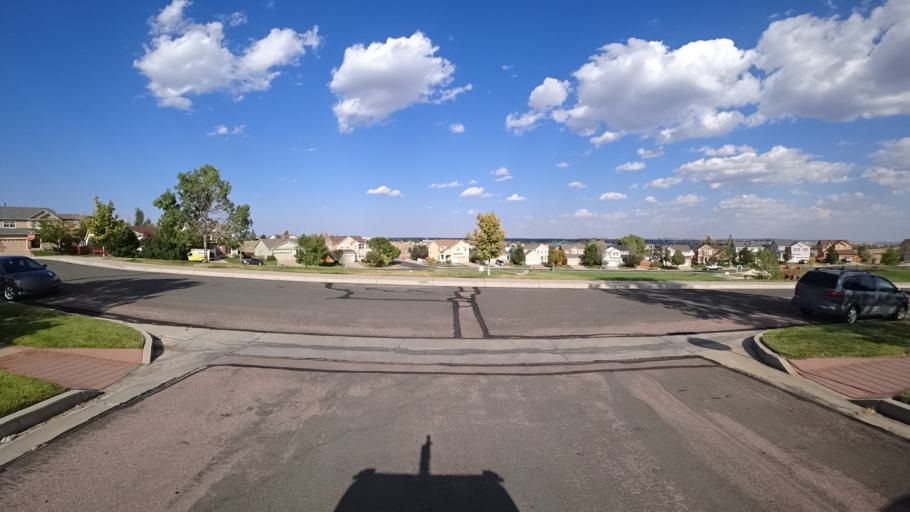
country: US
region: Colorado
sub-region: El Paso County
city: Cimarron Hills
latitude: 38.9110
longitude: -104.7255
